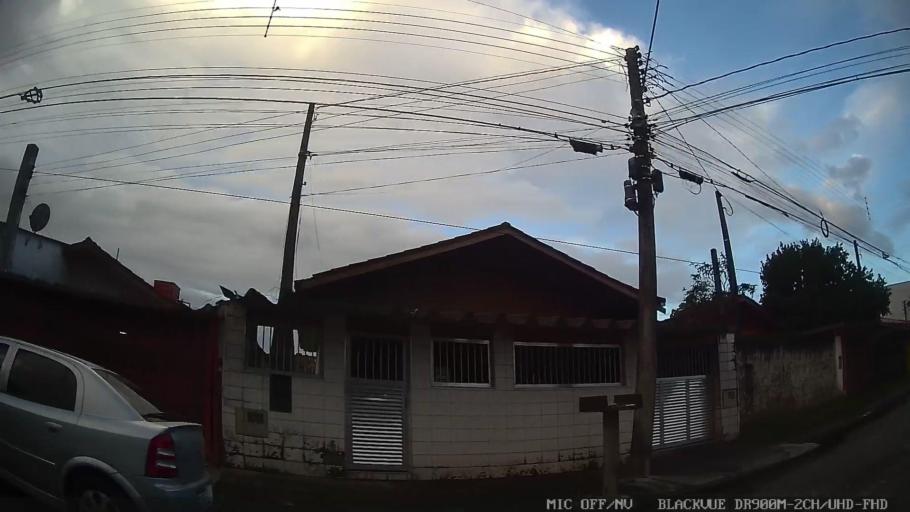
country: BR
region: Sao Paulo
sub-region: Itanhaem
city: Itanhaem
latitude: -24.1748
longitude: -46.7860
